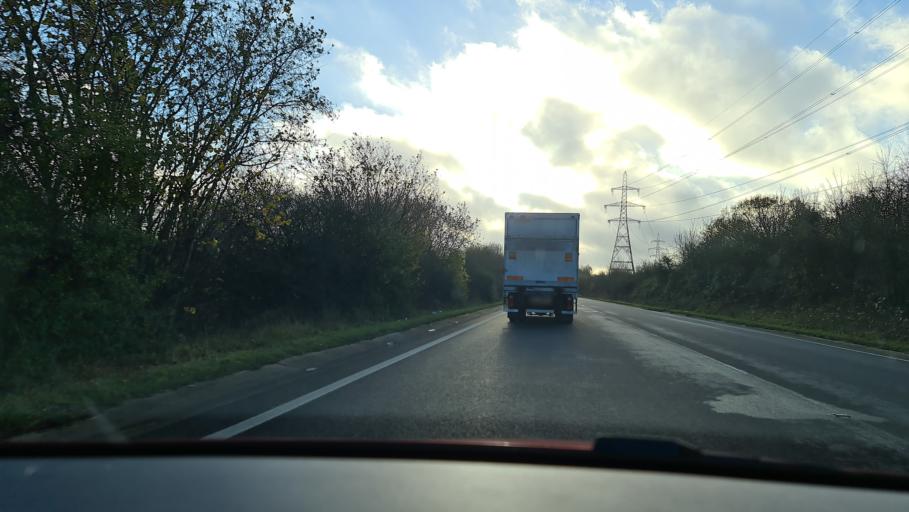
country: GB
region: England
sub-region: Buckinghamshire
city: Wendover
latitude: 51.7581
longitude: -0.7431
